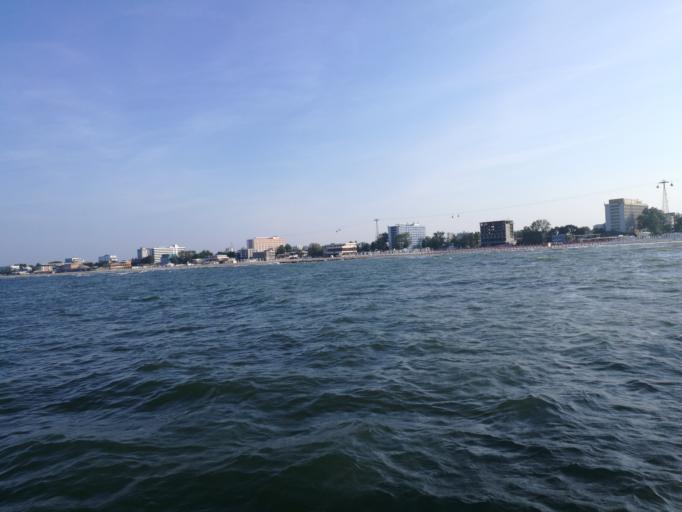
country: RO
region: Constanta
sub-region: Municipiul Constanta
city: Palazu Mare
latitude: 44.2316
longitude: 28.6332
